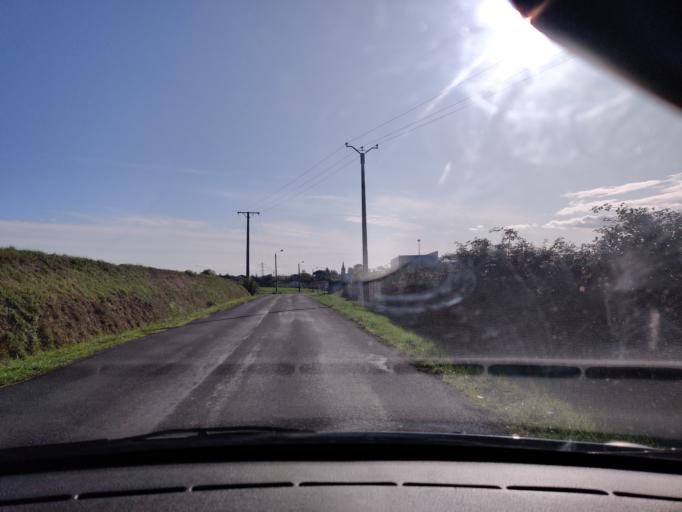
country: FR
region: Auvergne
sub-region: Departement du Puy-de-Dome
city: Aigueperse
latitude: 46.0273
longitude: 3.1909
